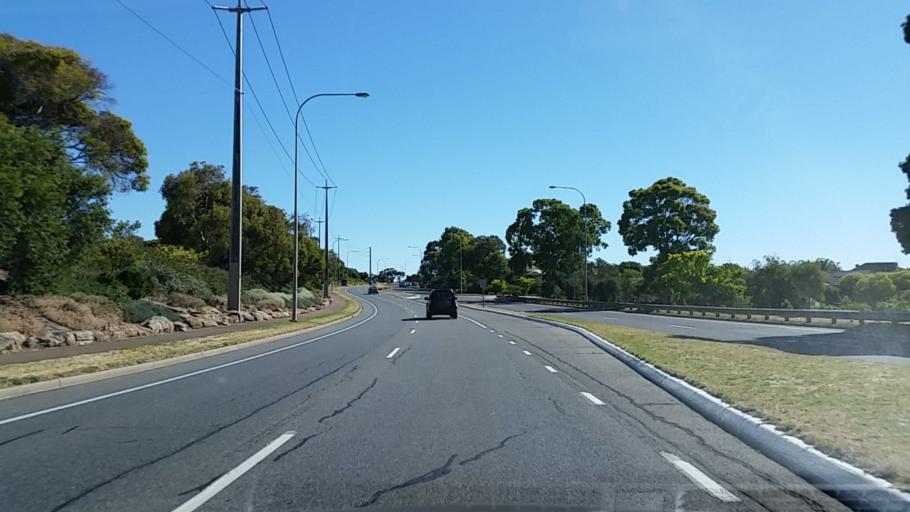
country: AU
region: South Australia
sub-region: Tea Tree Gully
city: Modbury
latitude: -34.8086
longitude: 138.6770
